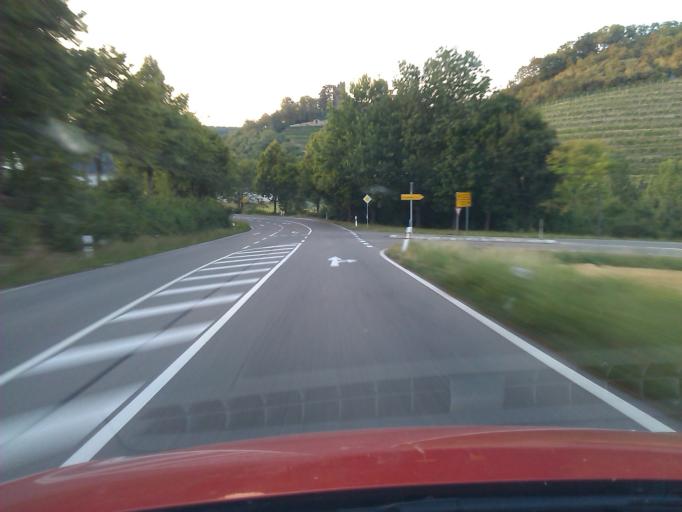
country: DE
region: Baden-Wuerttemberg
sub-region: Regierungsbezirk Stuttgart
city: Brackenheim
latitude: 49.0997
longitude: 9.0504
